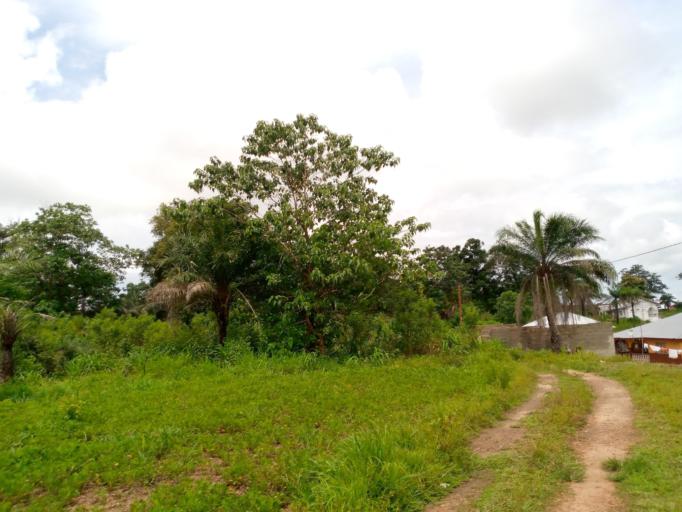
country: SL
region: Northern Province
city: Magburaka
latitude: 8.7272
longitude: -11.9322
